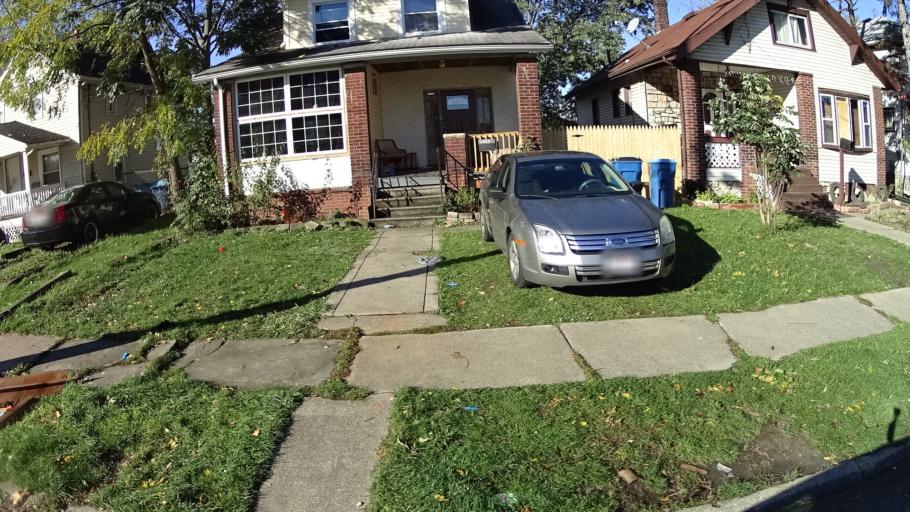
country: US
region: Ohio
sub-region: Lorain County
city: Lorain
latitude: 41.4446
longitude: -82.1636
